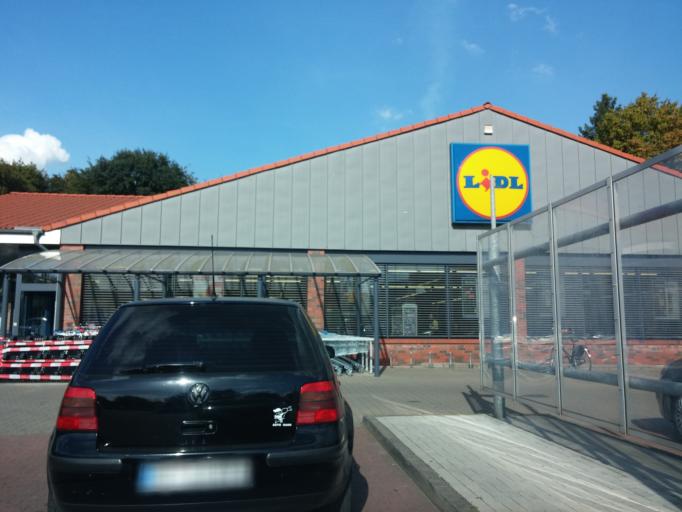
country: DE
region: North Rhine-Westphalia
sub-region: Regierungsbezirk Munster
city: Gladbeck
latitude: 51.5936
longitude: 6.9971
